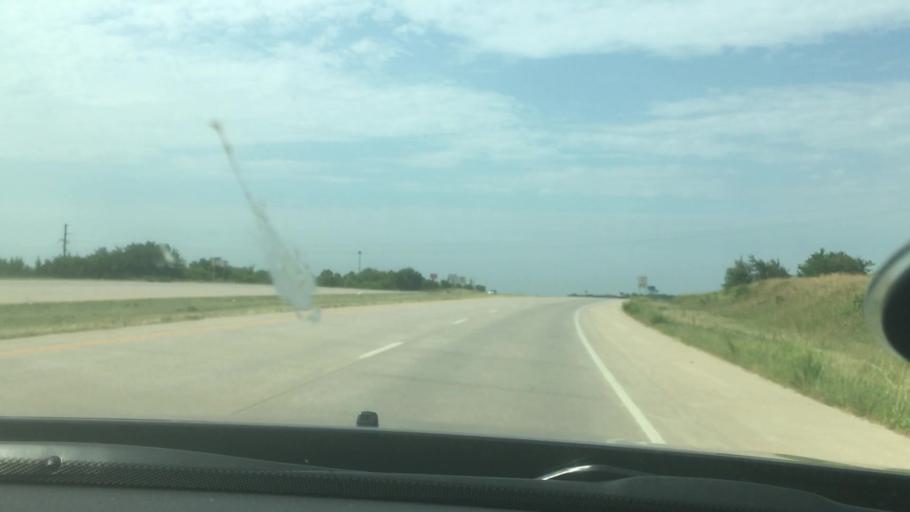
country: US
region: Oklahoma
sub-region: Pontotoc County
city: Ada
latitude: 34.7986
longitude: -96.6957
